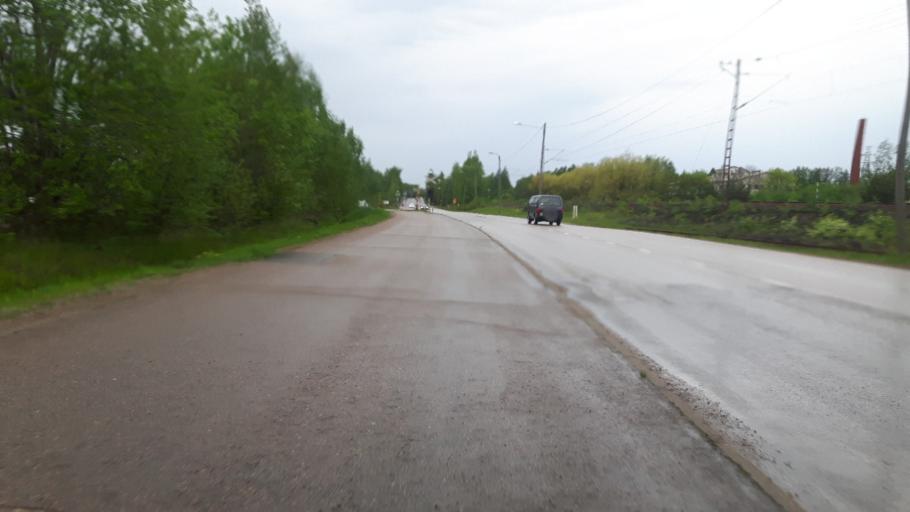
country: FI
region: Kymenlaakso
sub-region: Kotka-Hamina
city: Karhula
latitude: 60.5006
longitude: 26.9035
